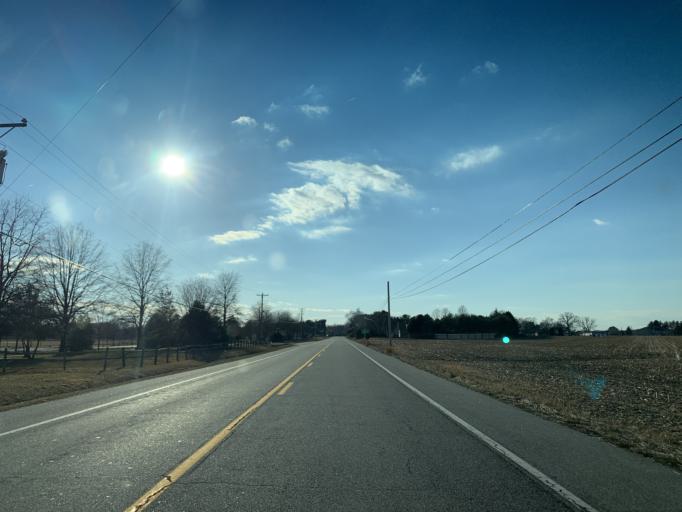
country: US
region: Maryland
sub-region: Queen Anne's County
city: Kingstown
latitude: 39.1490
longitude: -75.9720
